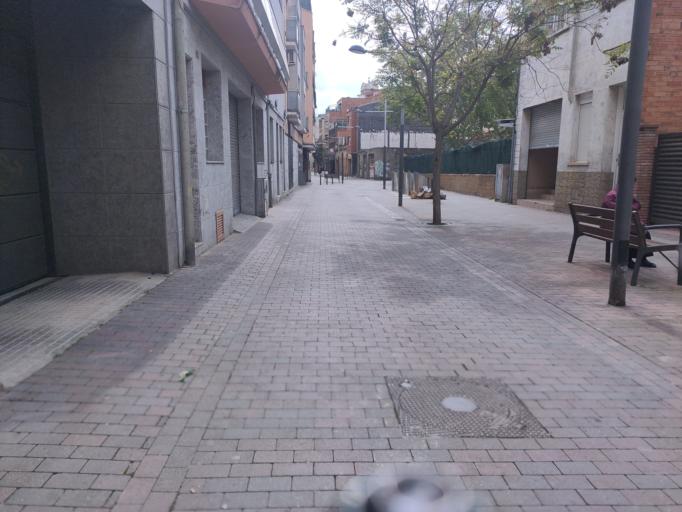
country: ES
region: Catalonia
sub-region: Provincia de Barcelona
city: Mollet del Valles
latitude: 41.5402
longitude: 2.2156
